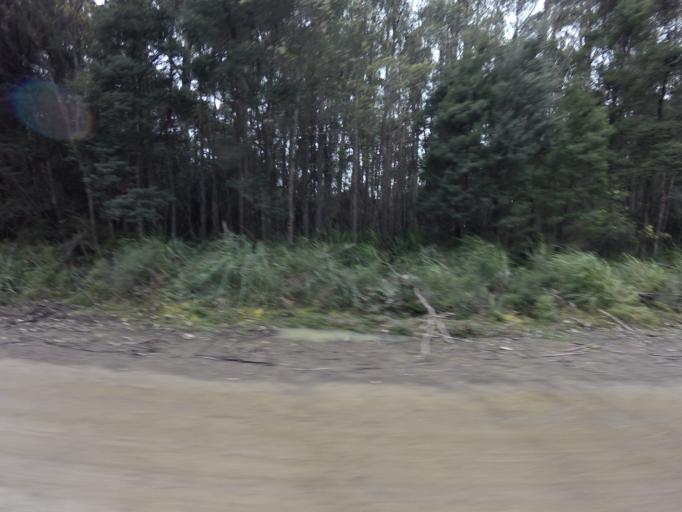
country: AU
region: Tasmania
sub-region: Huon Valley
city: Geeveston
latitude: -43.5133
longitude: 146.8853
